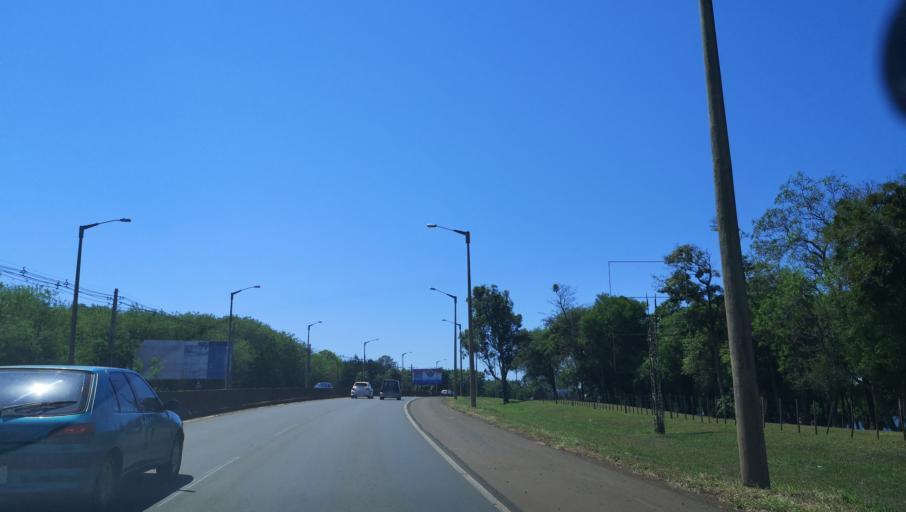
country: PY
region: Itapua
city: San Juan del Parana
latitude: -27.2917
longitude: -55.9169
